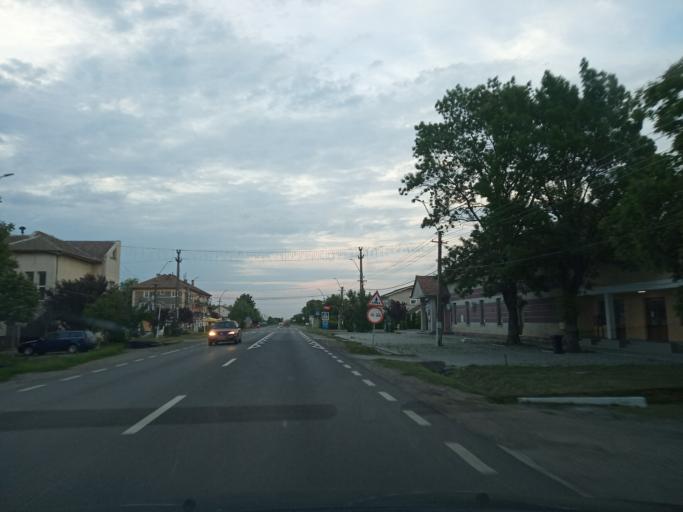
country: RO
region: Timis
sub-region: Comuna Voiteg
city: Voiteg
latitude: 45.4697
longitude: 21.2348
